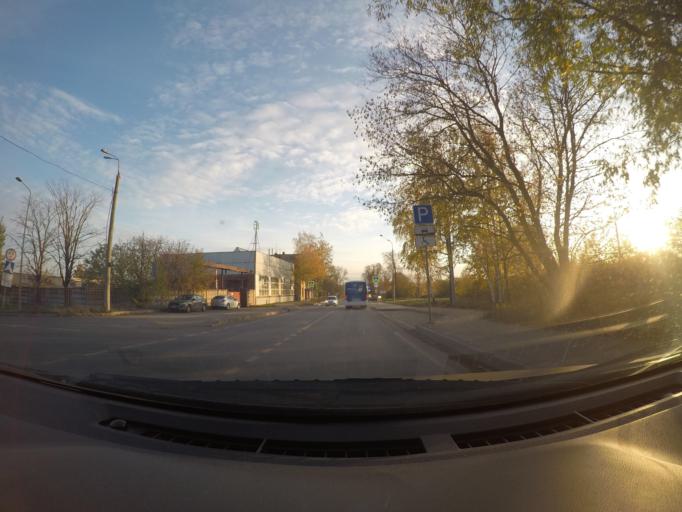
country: RU
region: Moskovskaya
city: Rzhavki
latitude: 55.9764
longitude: 37.2635
